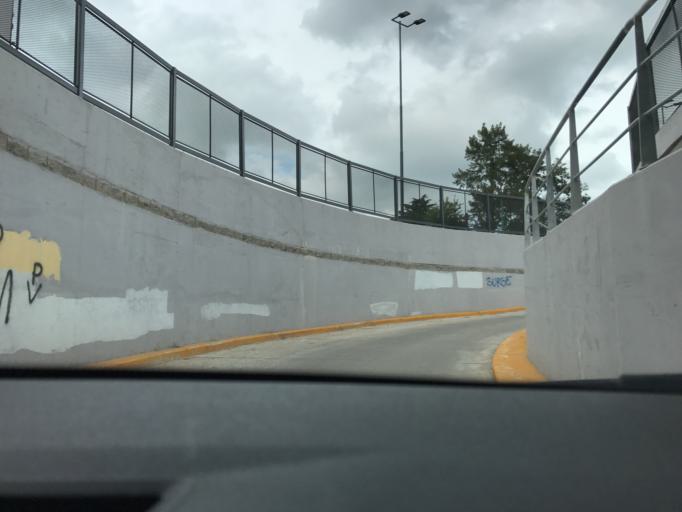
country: AR
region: Buenos Aires
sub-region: Partido de La Plata
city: La Plata
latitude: -34.8645
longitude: -58.0443
